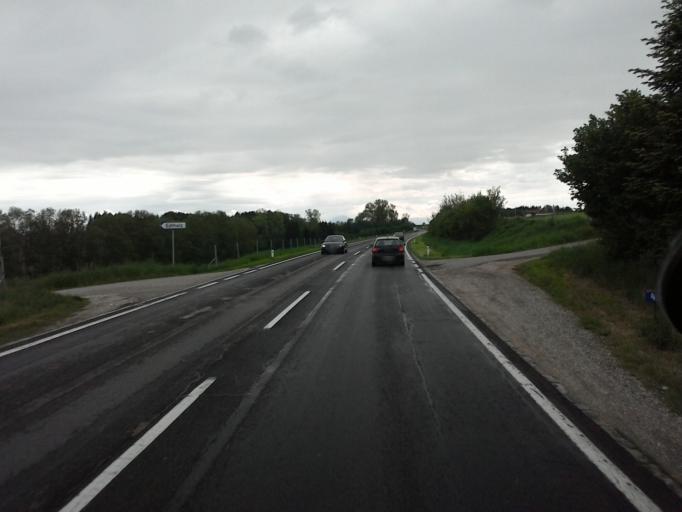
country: AT
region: Upper Austria
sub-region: Wels-Land
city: Thalheim bei Wels
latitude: 48.1240
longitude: 14.0499
